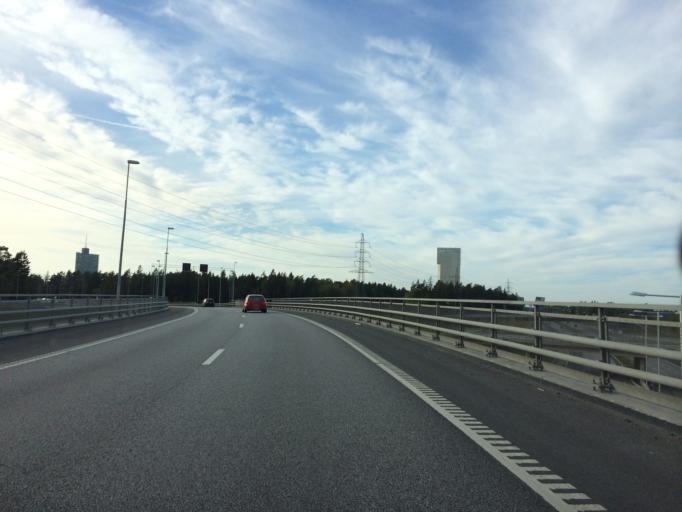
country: SE
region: Stockholm
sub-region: Stockholms Kommun
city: Kista
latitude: 59.4015
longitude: 17.9737
